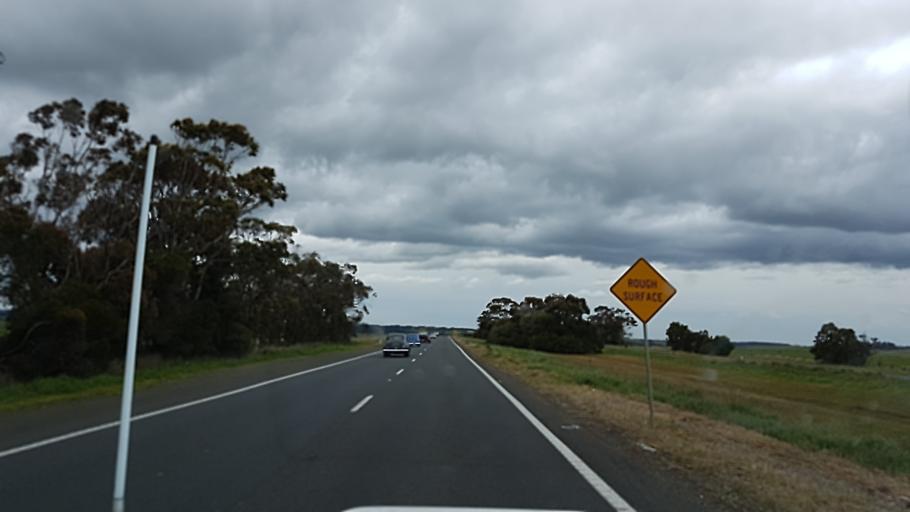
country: AU
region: Victoria
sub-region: Moorabool
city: Bacchus Marsh
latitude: -37.6016
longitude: 144.2755
